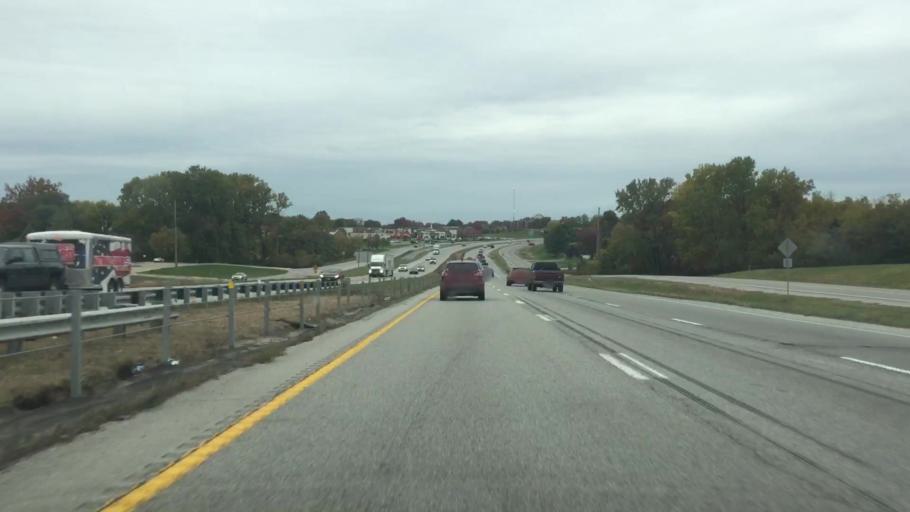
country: US
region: Missouri
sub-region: Jackson County
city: Lees Summit
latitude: 38.9131
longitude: -94.3960
